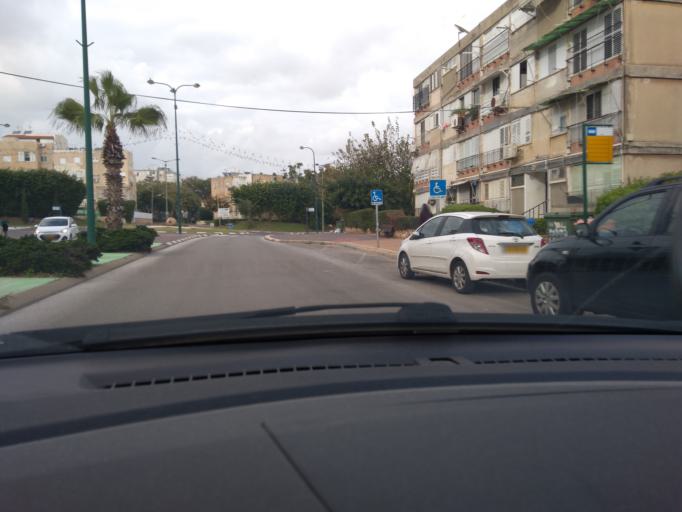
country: IL
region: Central District
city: Netanya
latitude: 32.3412
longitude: 34.8566
